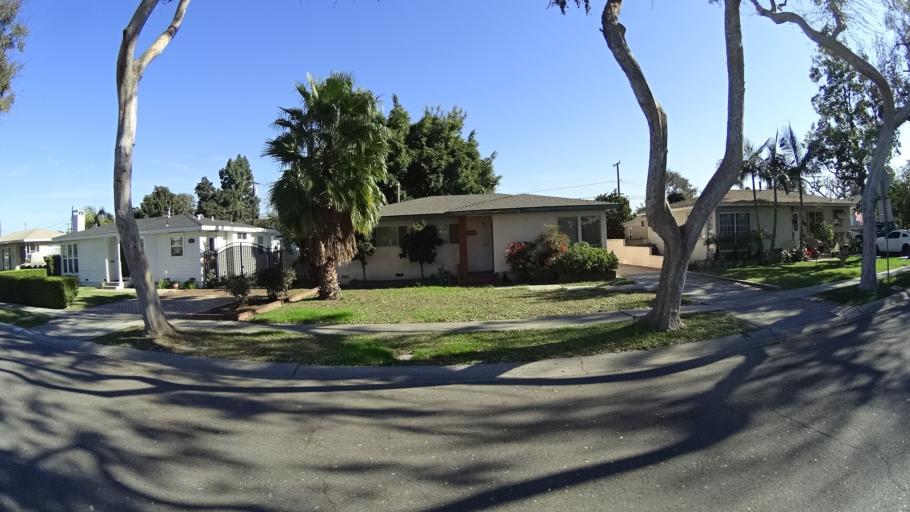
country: US
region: California
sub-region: Orange County
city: Garden Grove
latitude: 33.7839
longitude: -117.9384
